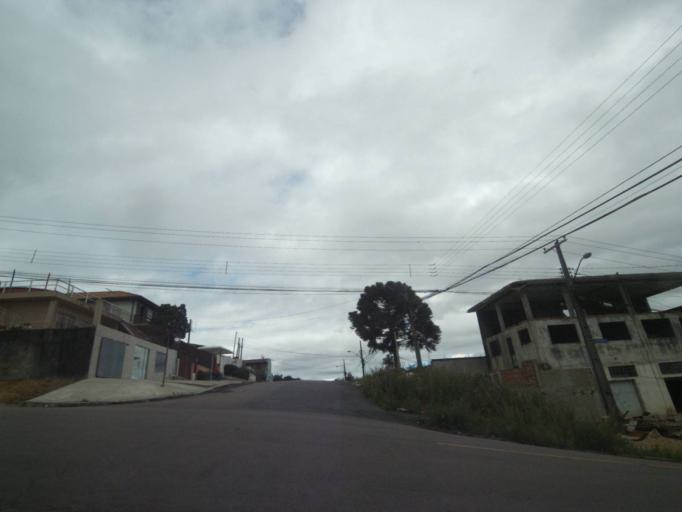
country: BR
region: Parana
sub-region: Curitiba
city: Curitiba
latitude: -25.4770
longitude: -49.2715
